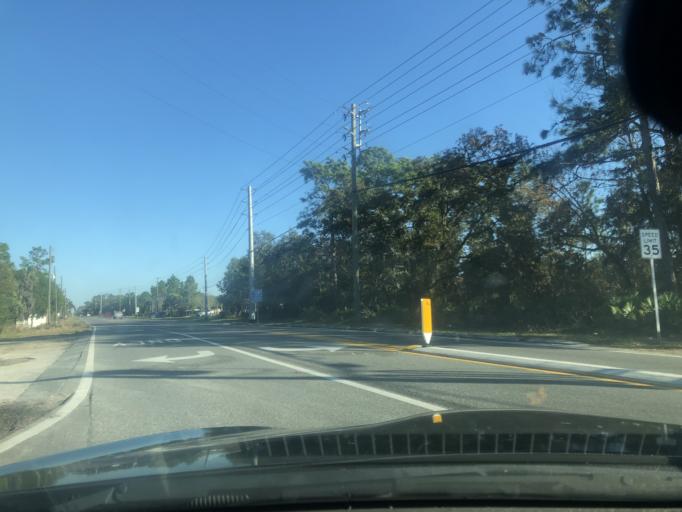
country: US
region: Florida
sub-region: Citrus County
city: Homosassa Springs
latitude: 28.7641
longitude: -82.5521
